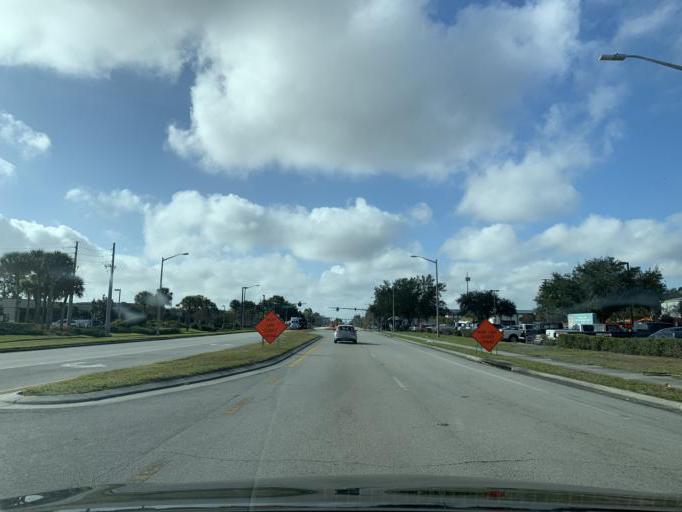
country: US
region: Florida
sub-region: Orange County
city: Oak Ridge
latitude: 28.5004
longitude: -81.4315
